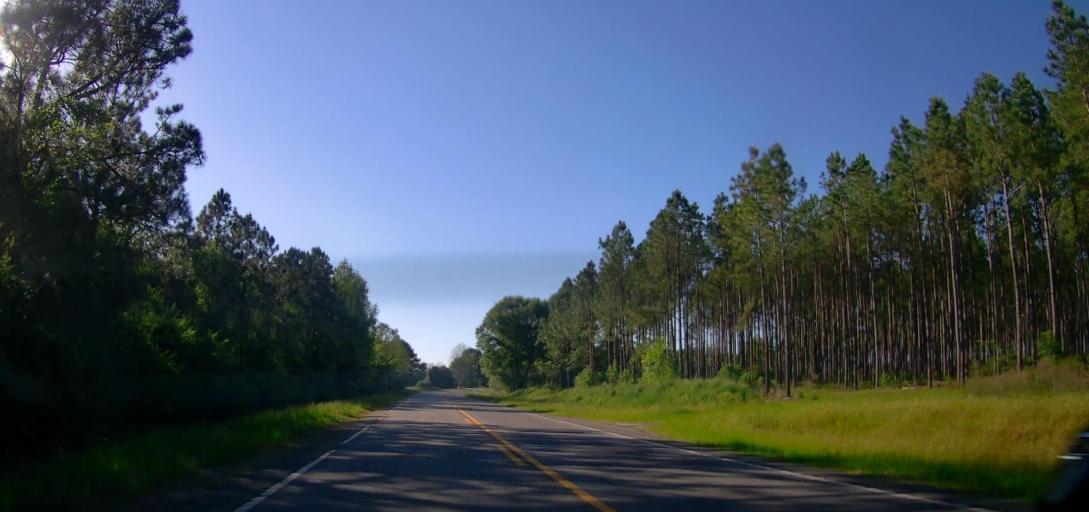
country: US
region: Georgia
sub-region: Ben Hill County
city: Fitzgerald
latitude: 31.7027
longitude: -83.3071
